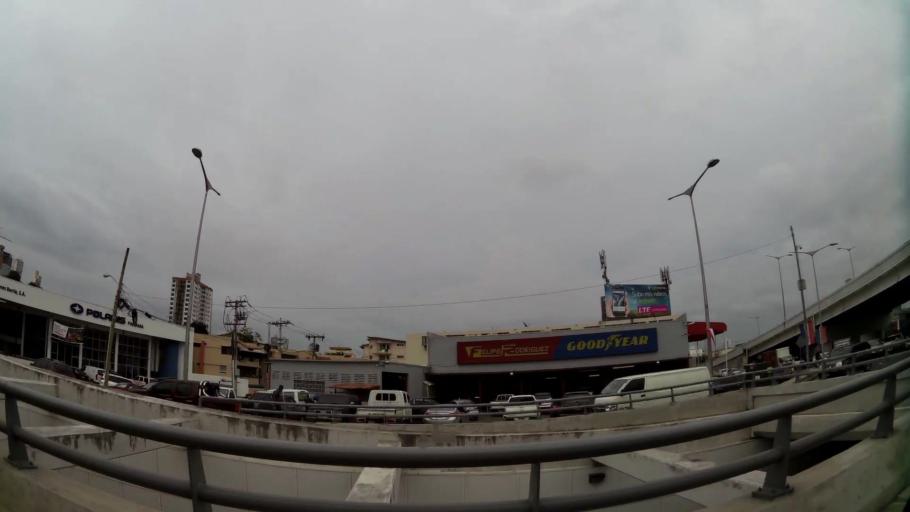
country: PA
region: Panama
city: Panama
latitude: 8.9961
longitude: -79.5282
